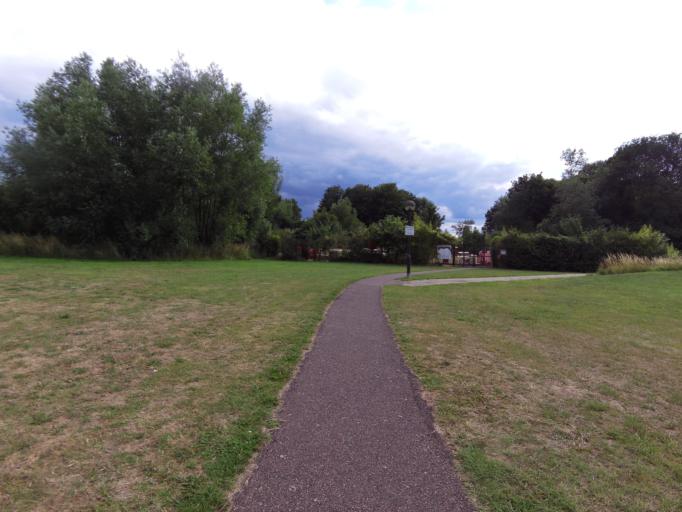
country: GB
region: England
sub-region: Hertfordshire
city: Broxbourne
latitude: 51.7428
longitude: -0.0094
